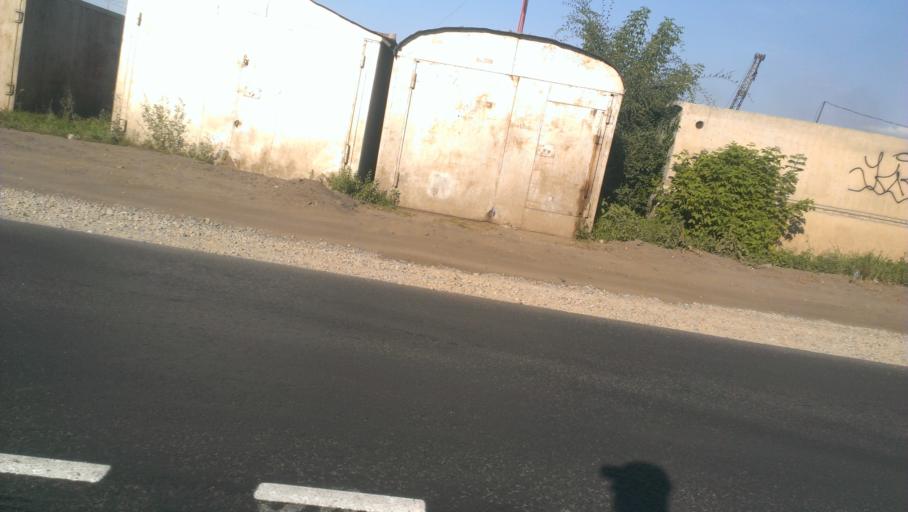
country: RU
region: Altai Krai
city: Novosilikatnyy
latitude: 53.3054
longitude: 83.6264
